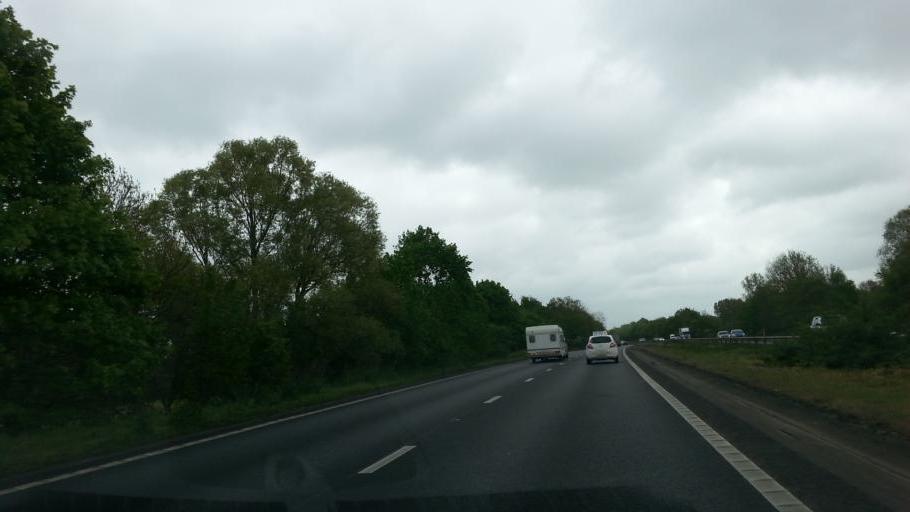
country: GB
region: England
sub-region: Suffolk
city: Bramford
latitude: 52.1236
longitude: 1.0998
